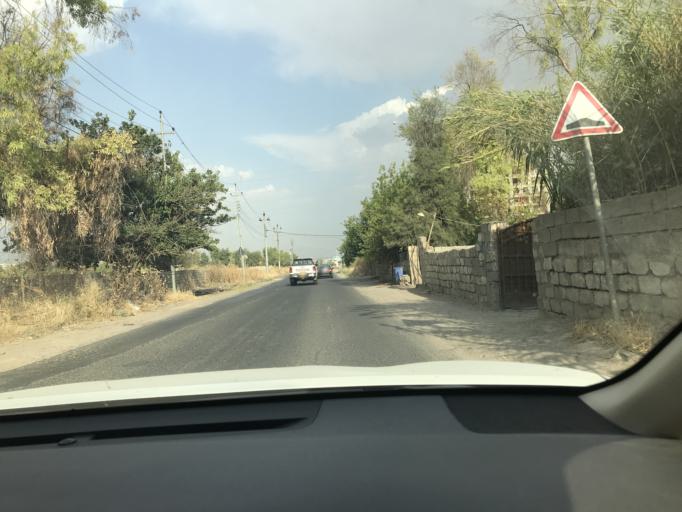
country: IQ
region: Arbil
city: Erbil
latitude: 36.2073
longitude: 43.9585
